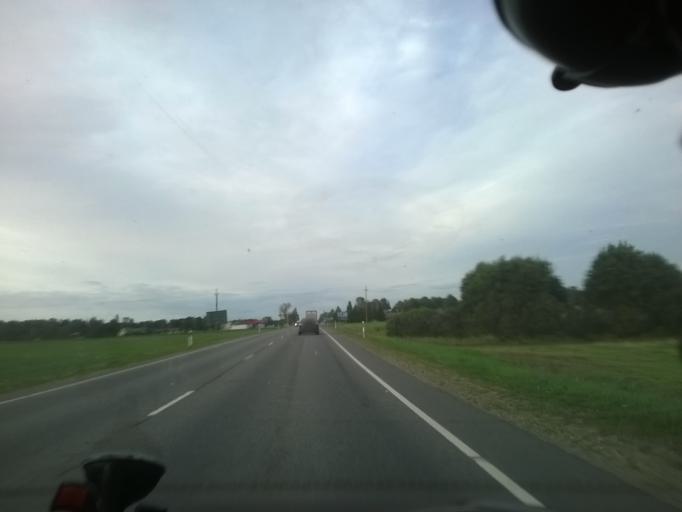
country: EE
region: Tartu
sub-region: UElenurme vald
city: Ulenurme
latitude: 58.0627
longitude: 26.7299
